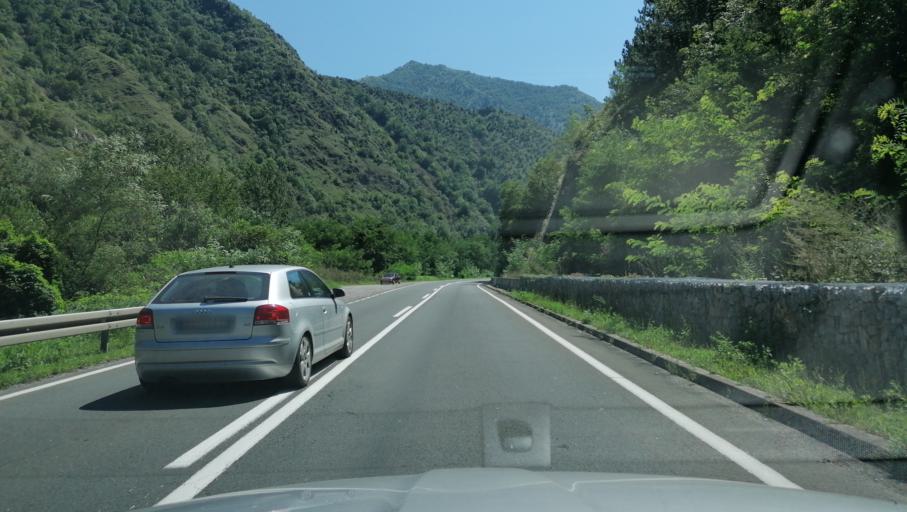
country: RS
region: Central Serbia
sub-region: Raski Okrug
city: Kraljevo
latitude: 43.6202
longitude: 20.5523
